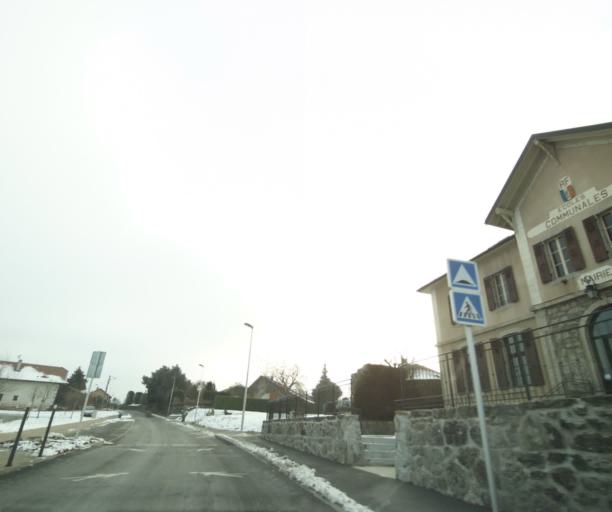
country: FR
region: Rhone-Alpes
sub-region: Departement de la Haute-Savoie
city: Arthaz-Pont-Notre-Dame
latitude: 46.1475
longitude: 6.2368
